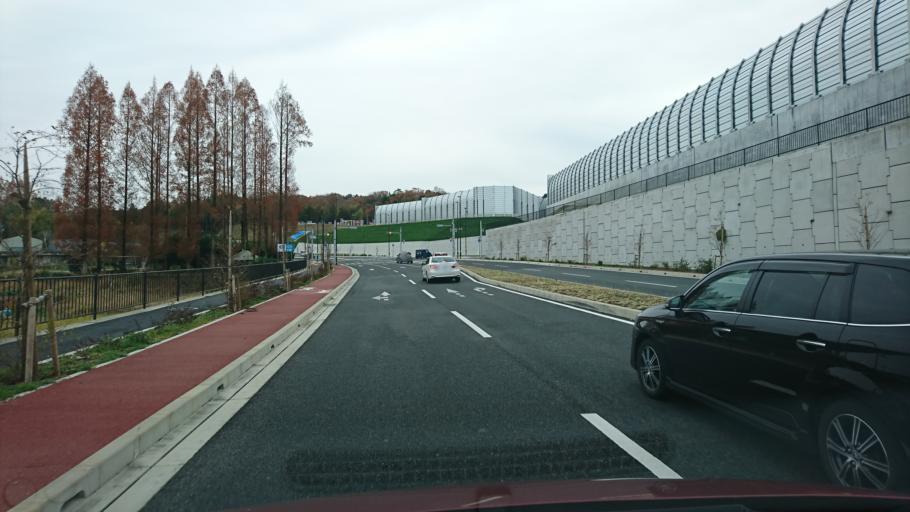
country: JP
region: Osaka
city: Ikeda
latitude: 34.8828
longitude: 135.4068
